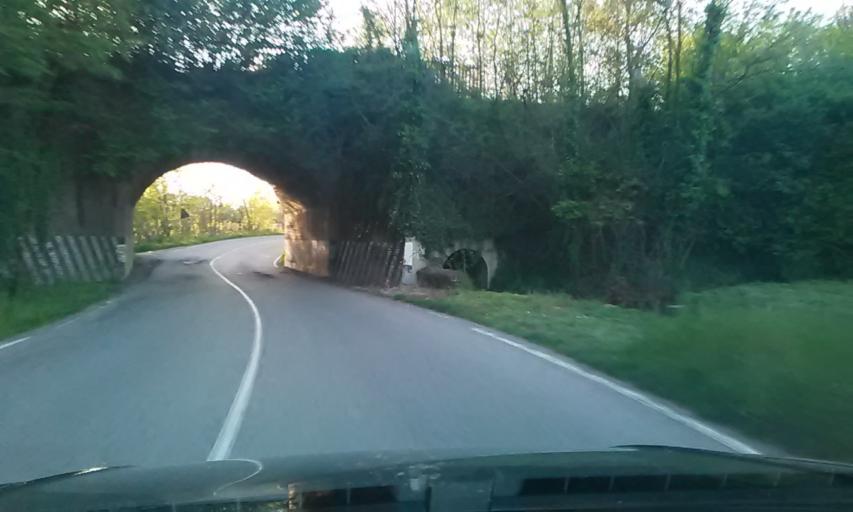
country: IT
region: Piedmont
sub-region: Provincia di Vercelli
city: Rovasenda
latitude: 45.5337
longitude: 8.3143
